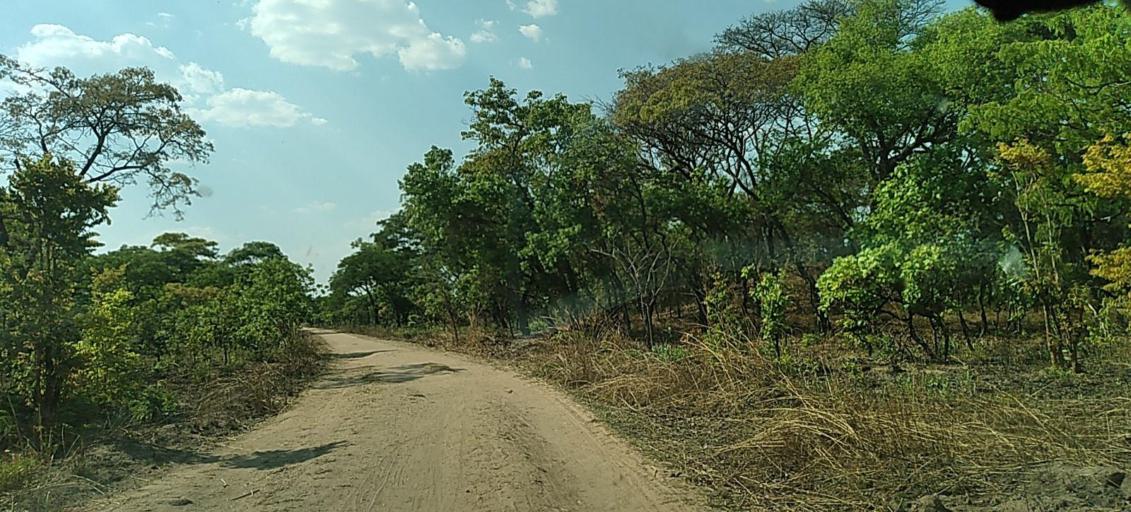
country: ZM
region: North-Western
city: Kalengwa
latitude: -13.1027
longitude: 24.9872
